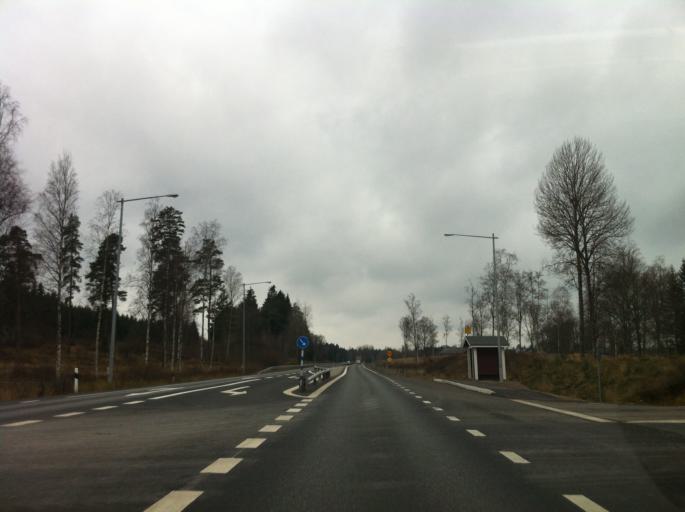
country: SE
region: Joenkoeping
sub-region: Vetlanda Kommun
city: Vetlanda
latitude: 57.4264
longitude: 15.1434
